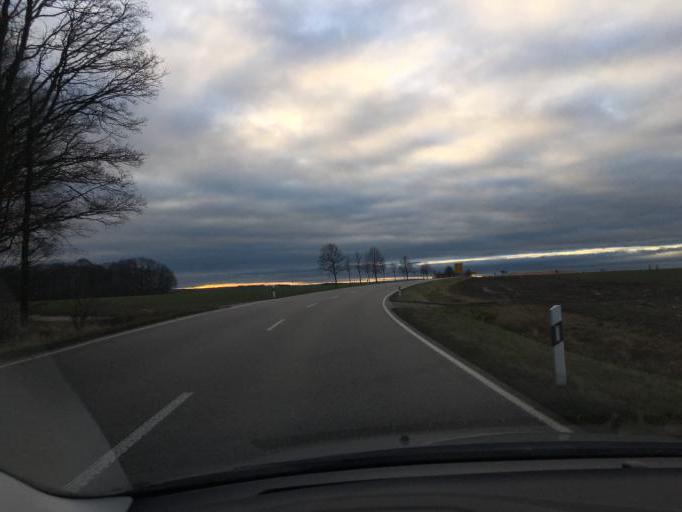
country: DE
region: Saxony
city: Frohburg
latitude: 51.0220
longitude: 12.5568
